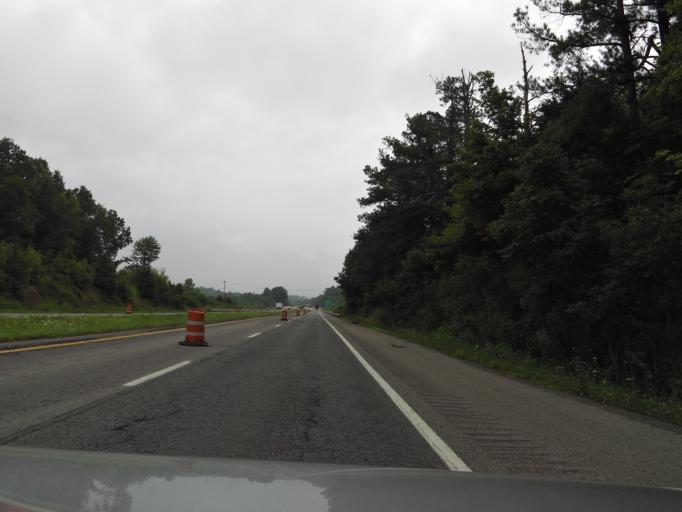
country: US
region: Kentucky
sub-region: Muhlenberg County
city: Morehead
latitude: 37.2737
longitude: -87.1468
